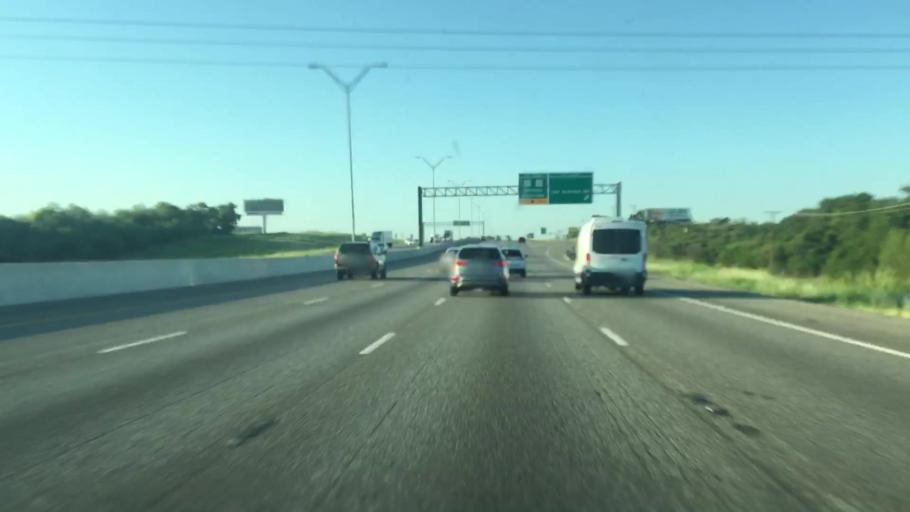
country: US
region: Texas
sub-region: Hill County
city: Hillsboro
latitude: 32.0282
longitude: -97.0956
